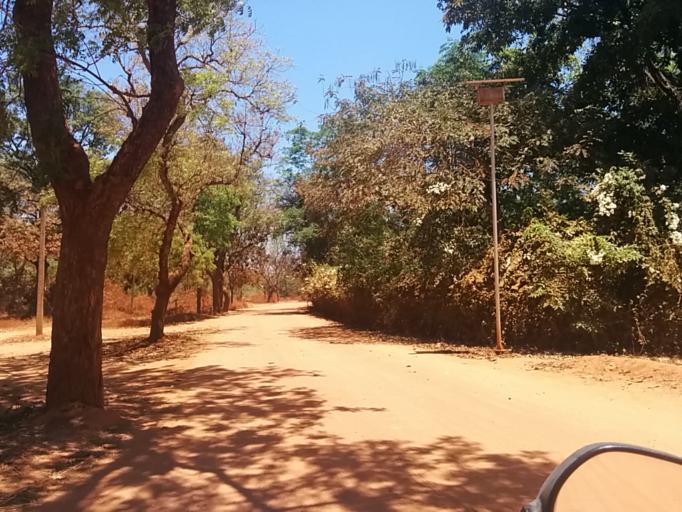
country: IN
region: Tamil Nadu
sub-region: Villupuram
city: Auroville
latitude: 12.0067
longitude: 79.8080
